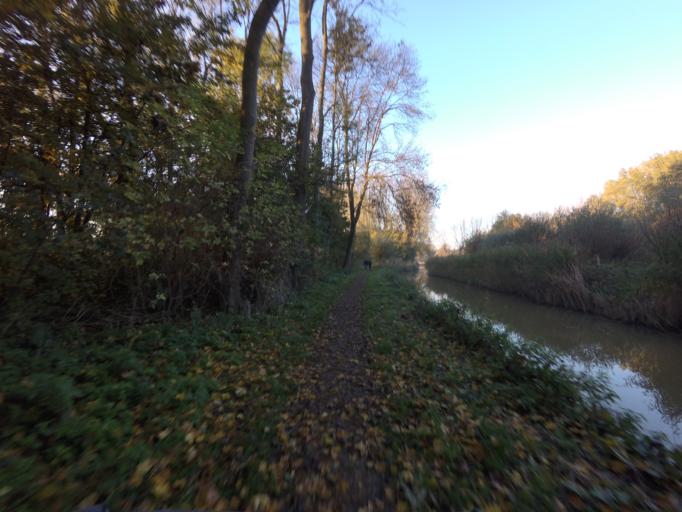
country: NL
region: North Brabant
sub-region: Gemeente Woudrichem
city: Woudrichem
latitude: 51.7900
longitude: 5.0217
